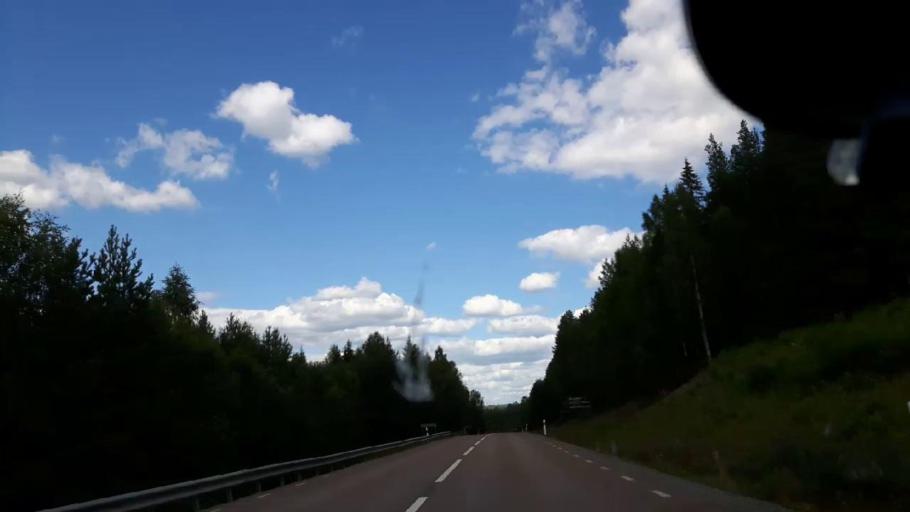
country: SE
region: Jaemtland
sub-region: Ragunda Kommun
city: Hammarstrand
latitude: 62.9911
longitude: 16.6771
